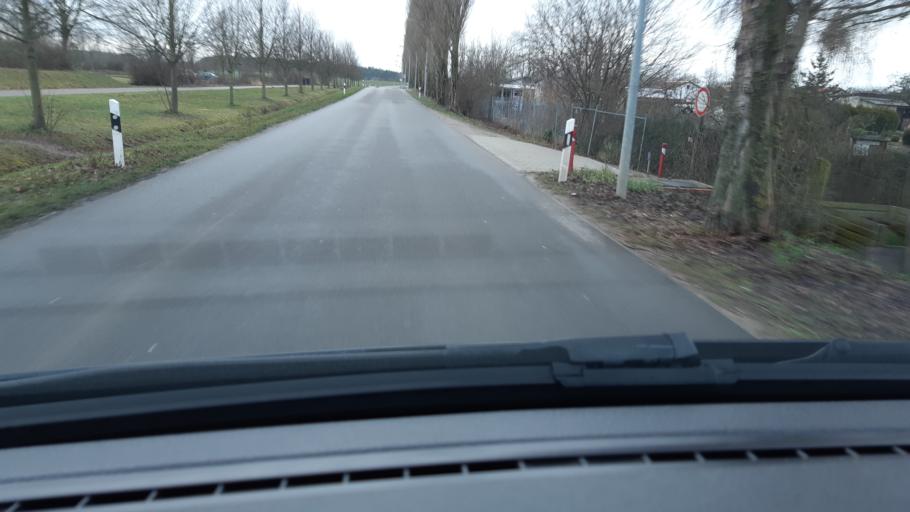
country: DE
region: Brandenburg
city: Templin
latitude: 53.1112
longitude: 13.5106
